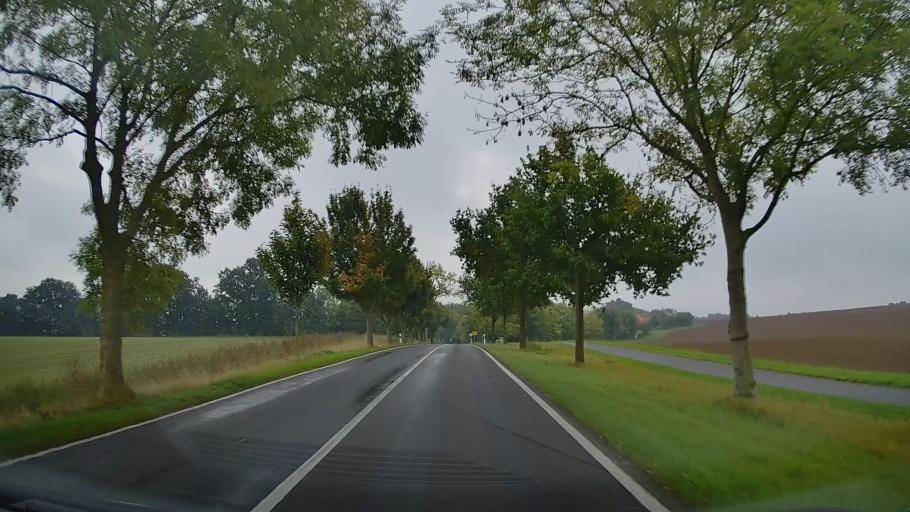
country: DE
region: Mecklenburg-Vorpommern
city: Ostseebad Boltenhagen
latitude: 53.9425
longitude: 11.2388
